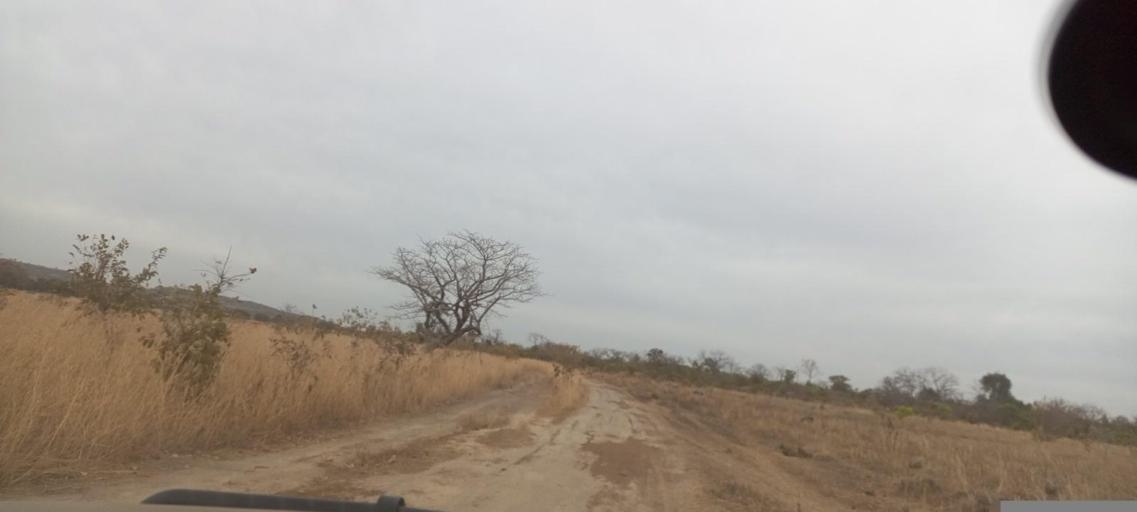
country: ML
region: Koulikoro
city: Kati
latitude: 12.7703
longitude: -8.3833
